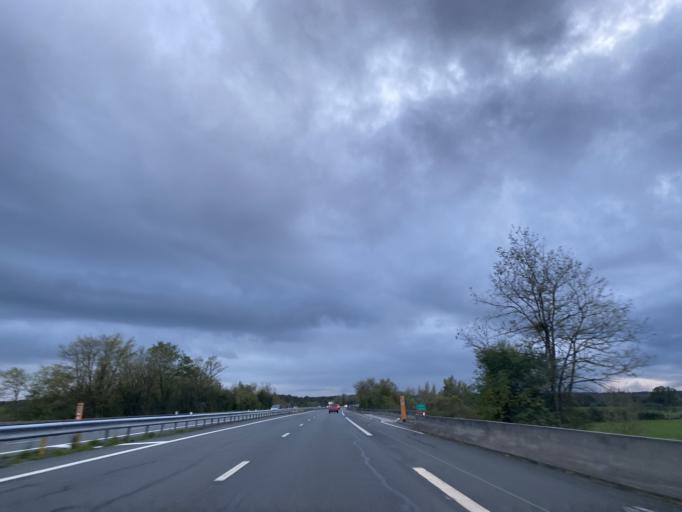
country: FR
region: Centre
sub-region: Departement du Cher
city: Orval
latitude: 46.7857
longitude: 2.4120
